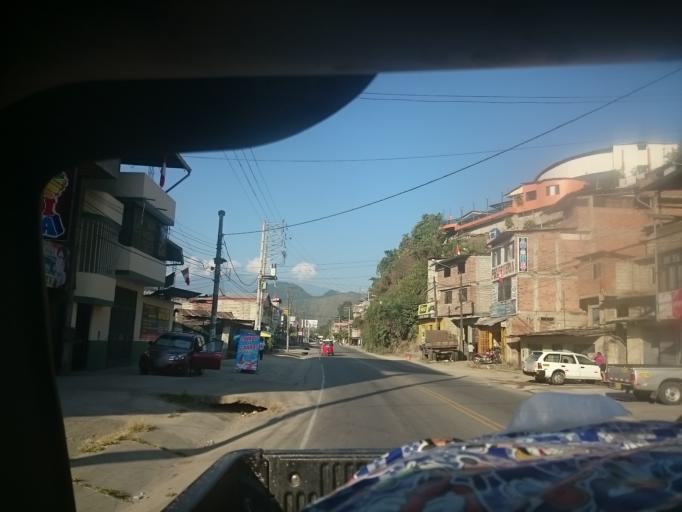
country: PE
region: Junin
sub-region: Chanchamayo
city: La Merced
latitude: -11.0547
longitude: -75.3247
